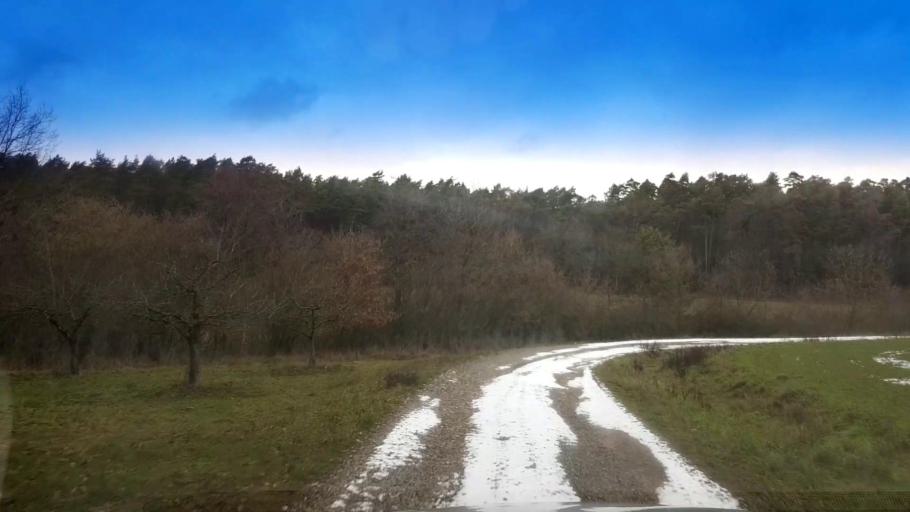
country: DE
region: Bavaria
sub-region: Upper Franconia
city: Lauter
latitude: 49.9554
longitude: 10.7701
